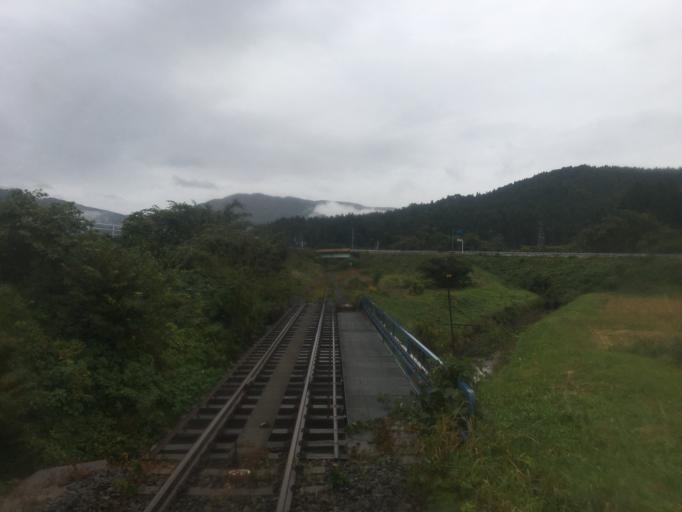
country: JP
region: Yamagata
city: Tsuruoka
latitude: 38.7902
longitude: 139.9978
